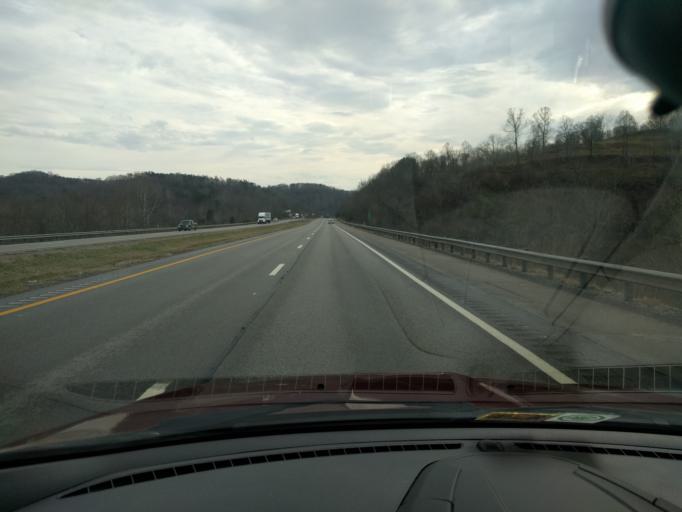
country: US
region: West Virginia
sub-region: Wood County
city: Mineral Wells
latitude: 39.1208
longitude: -81.5463
